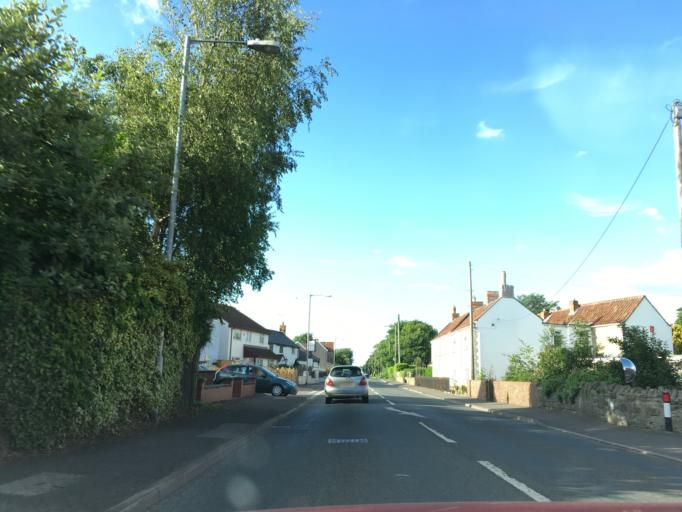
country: GB
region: England
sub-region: Somerset
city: Highbridge
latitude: 51.2045
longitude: -2.9883
